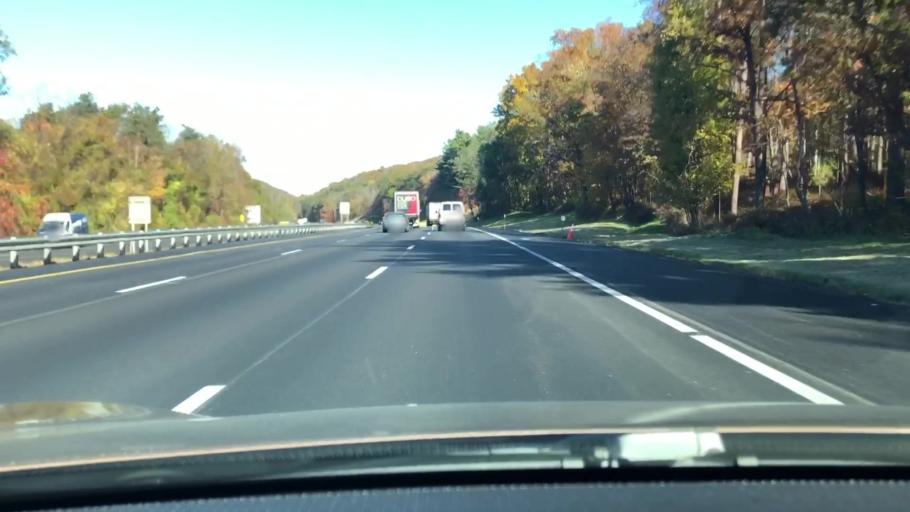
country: US
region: New York
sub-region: Rockland County
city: Sloatsburg
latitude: 41.2330
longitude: -74.1753
